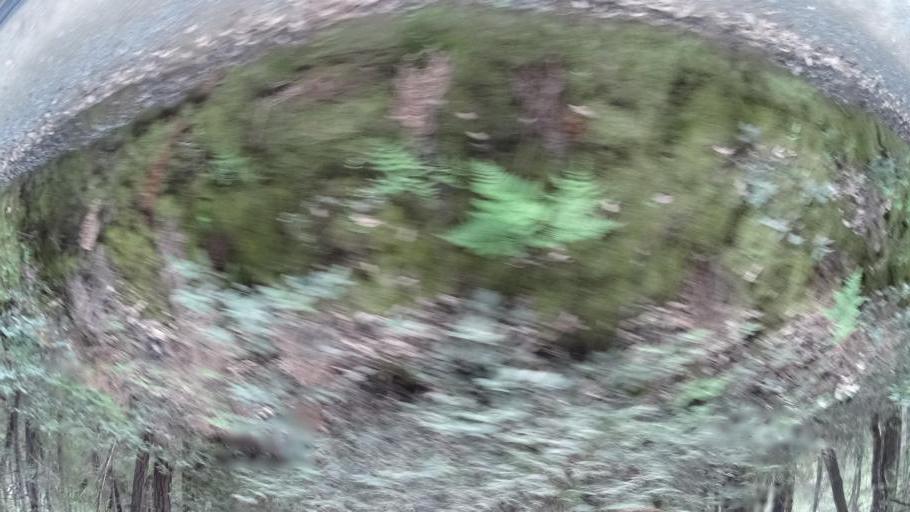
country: US
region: California
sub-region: Humboldt County
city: Redway
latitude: 40.0446
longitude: -123.8409
